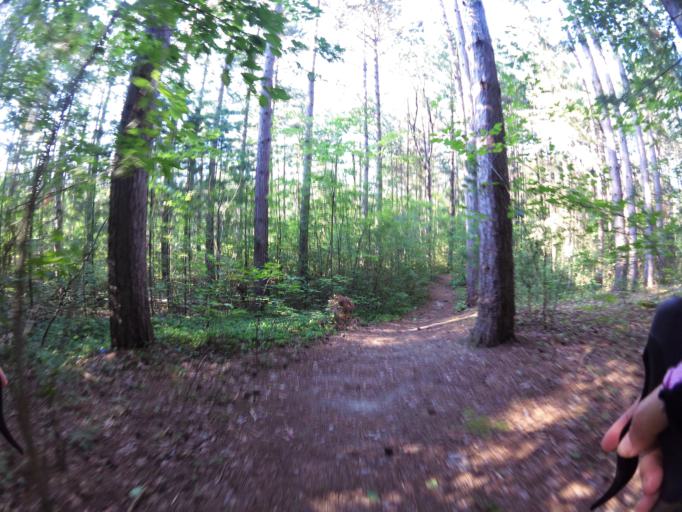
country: CA
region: Ontario
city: Bells Corners
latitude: 45.3198
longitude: -75.7334
